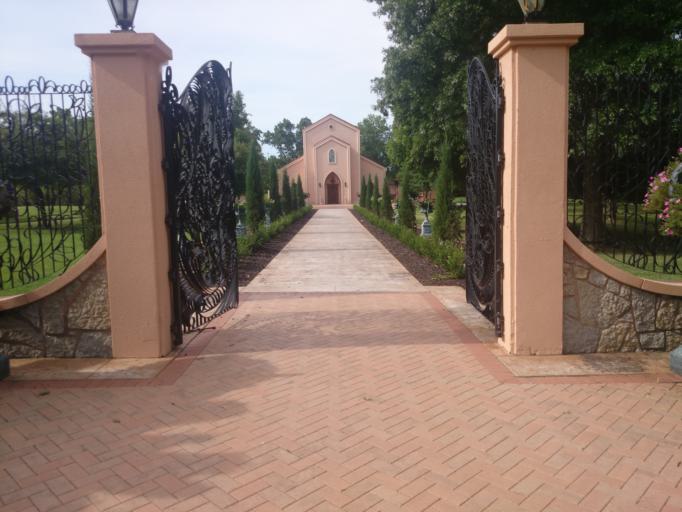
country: US
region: Missouri
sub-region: Jasper County
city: Duenweg
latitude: 37.1112
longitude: -94.3468
